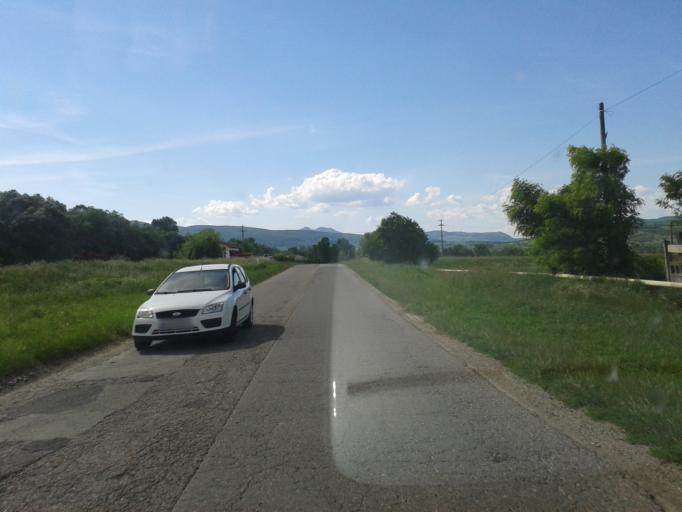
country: RO
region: Hunedoara
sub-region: Comuna Geoagiu
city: Geoagiu
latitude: 45.8898
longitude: 23.2344
